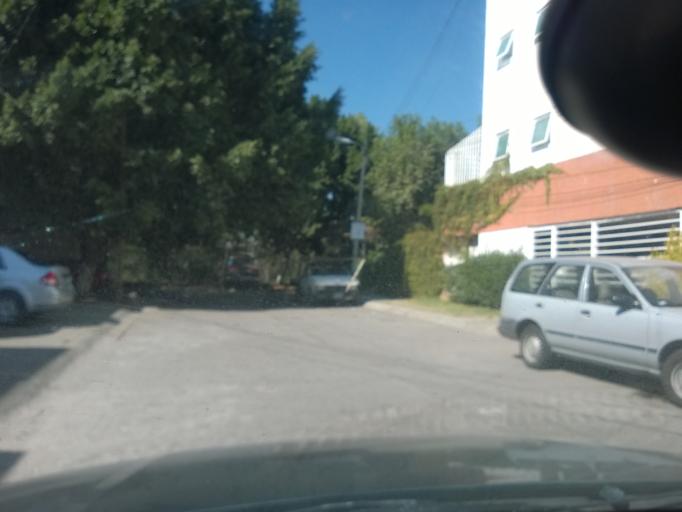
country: MX
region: Guanajuato
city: Leon
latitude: 21.1573
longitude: -101.6845
